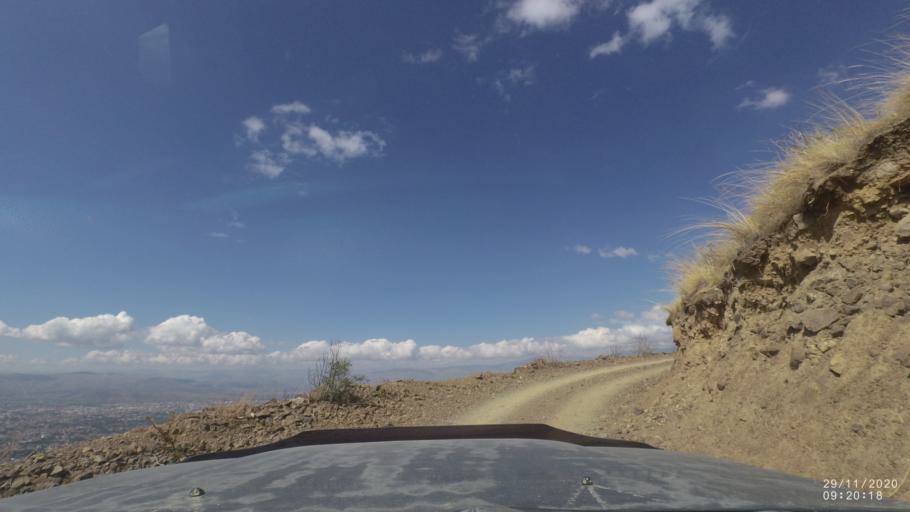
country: BO
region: Cochabamba
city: Cochabamba
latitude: -17.3242
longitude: -66.1856
